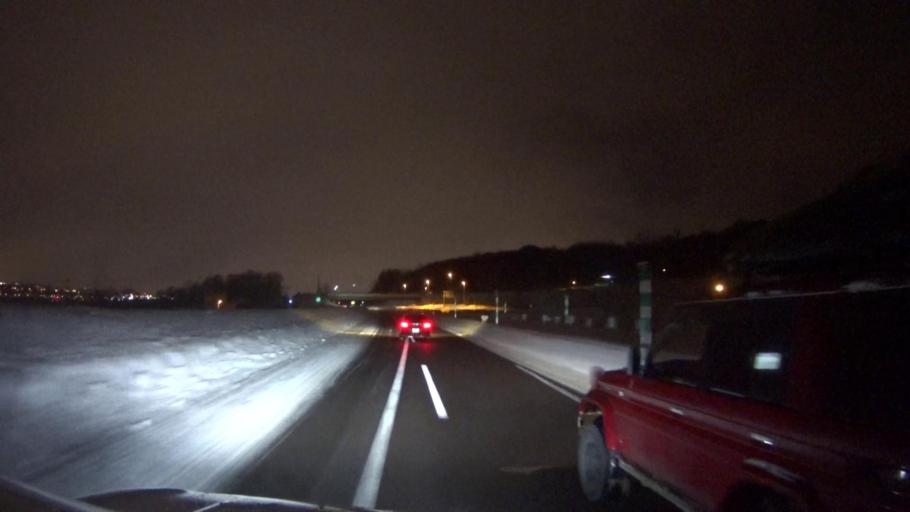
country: JP
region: Hokkaido
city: Otaru
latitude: 43.1334
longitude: 141.1730
